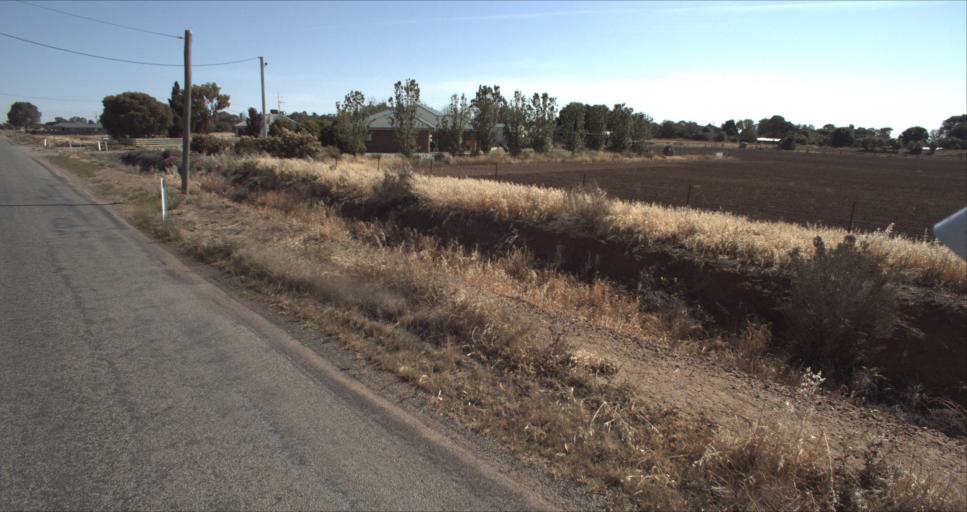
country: AU
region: New South Wales
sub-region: Leeton
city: Leeton
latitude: -34.5403
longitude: 146.4192
